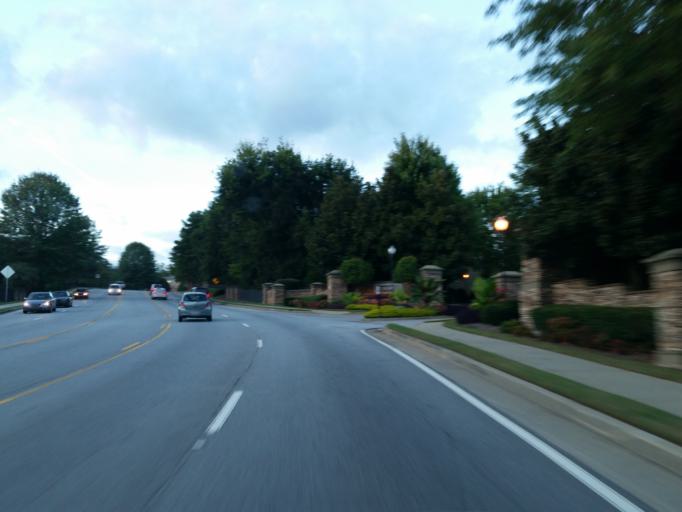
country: US
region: Georgia
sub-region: Cobb County
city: Vinings
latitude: 33.8521
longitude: -84.4813
